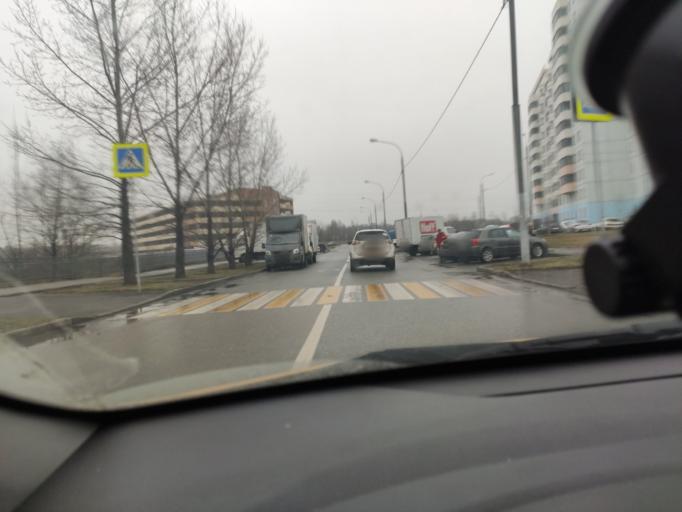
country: RU
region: Moskovskaya
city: Shcherbinka
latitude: 55.5024
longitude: 37.5878
